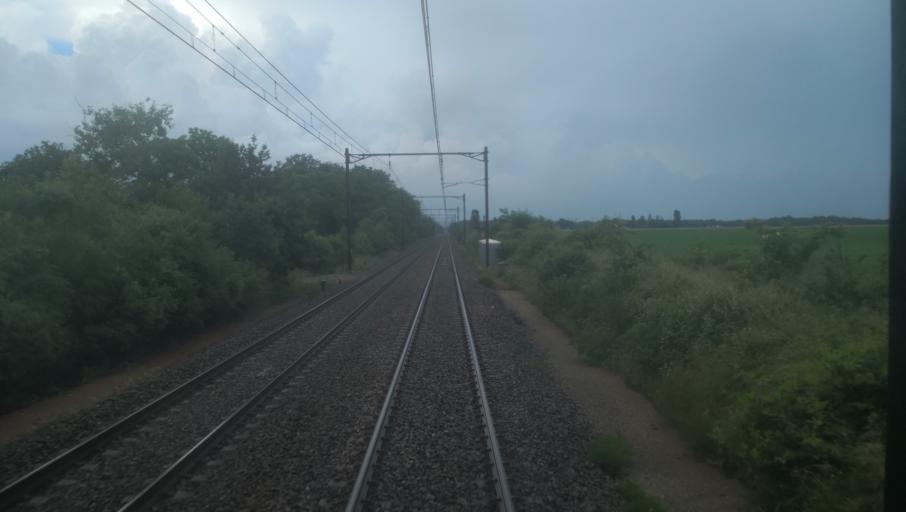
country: FR
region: Centre
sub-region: Departement du Loiret
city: Saint-Cyr-en-Val
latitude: 47.7958
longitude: 1.9430
